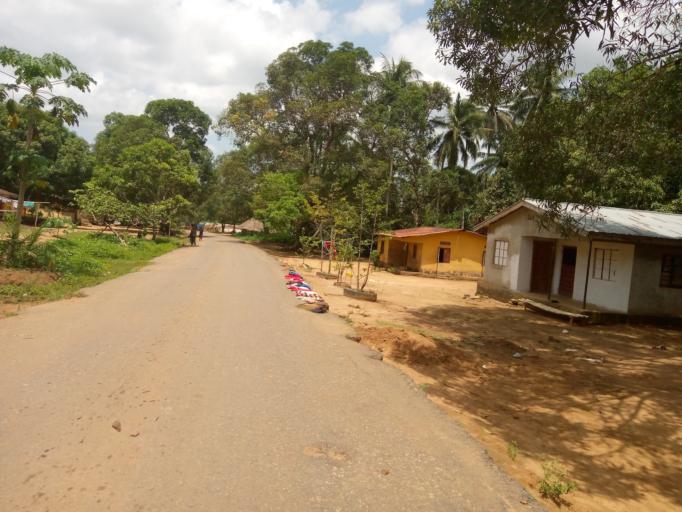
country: SL
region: Western Area
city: Waterloo
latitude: 8.3794
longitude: -12.9594
